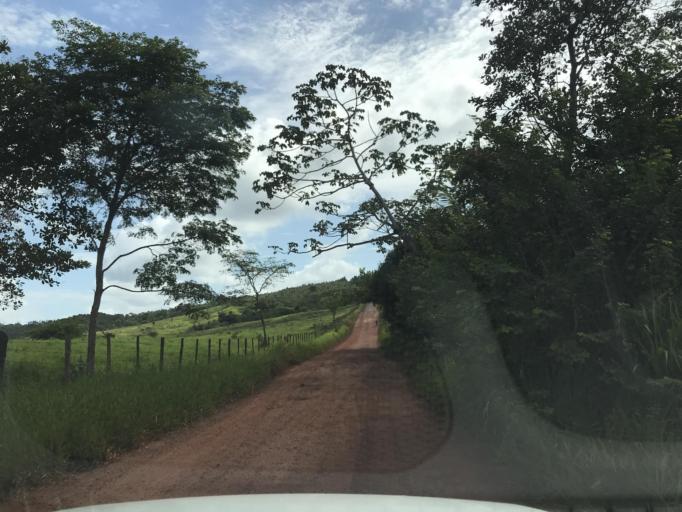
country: BR
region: Bahia
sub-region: Entre Rios
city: Entre Rios
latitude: -12.1750
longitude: -38.1168
